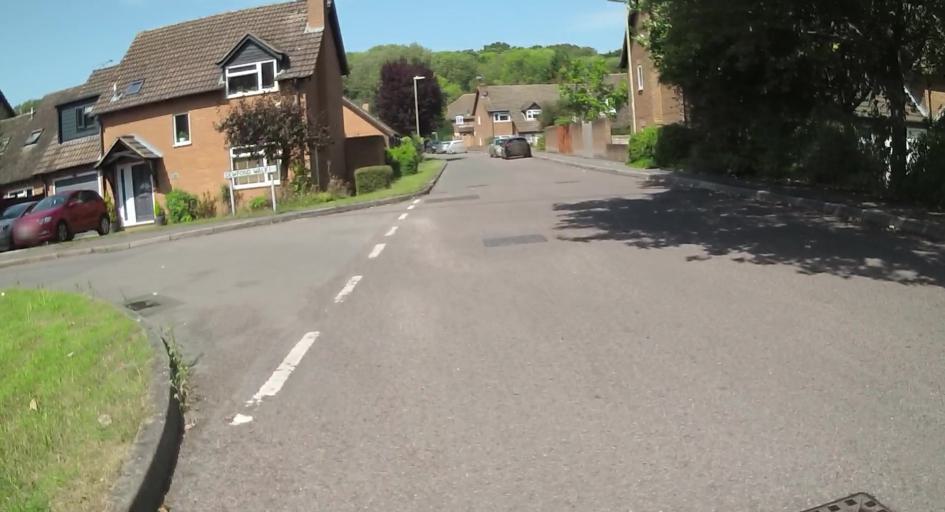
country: GB
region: England
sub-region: Hampshire
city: Old Basing
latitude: 51.2782
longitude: -1.0590
